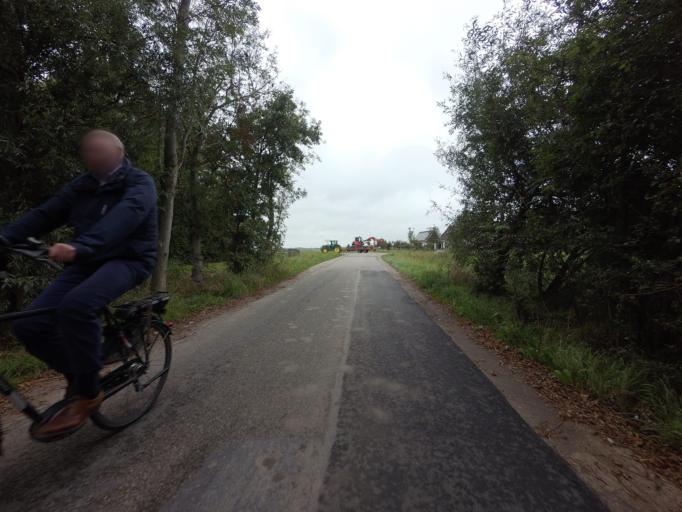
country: NL
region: Zeeland
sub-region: Gemeente Vlissingen
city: Vlissingen
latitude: 51.4897
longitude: 3.5567
